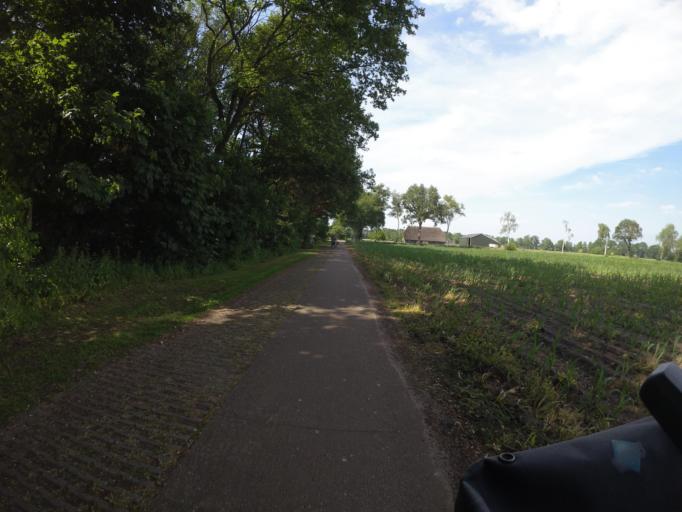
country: NL
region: Overijssel
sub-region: Gemeente Raalte
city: Raalte
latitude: 52.4410
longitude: 6.3059
